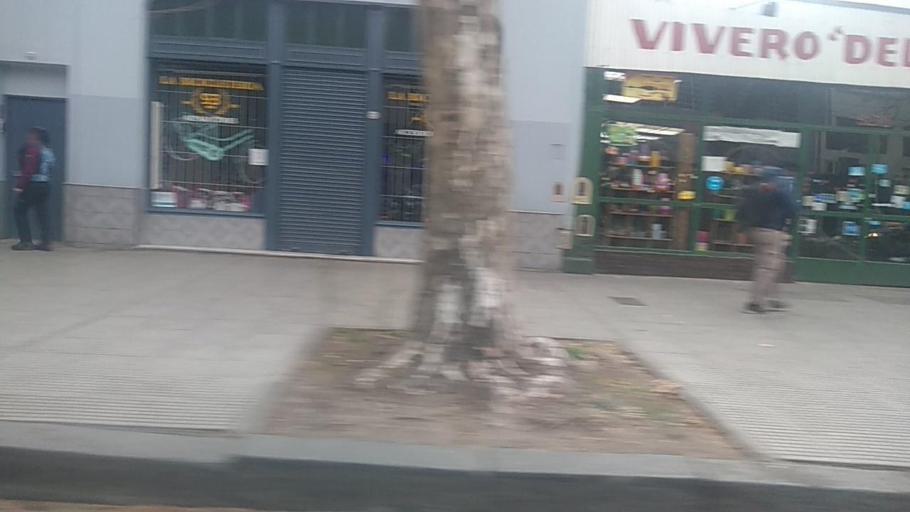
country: AR
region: Buenos Aires F.D.
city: Villa Santa Rita
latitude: -34.5977
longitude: -58.4986
